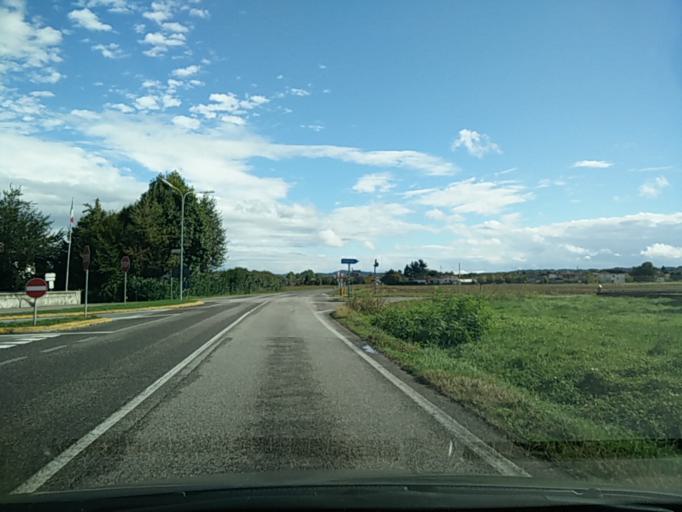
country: IT
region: Veneto
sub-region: Provincia di Treviso
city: Moriago della Battaglia
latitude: 45.8655
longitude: 12.1137
